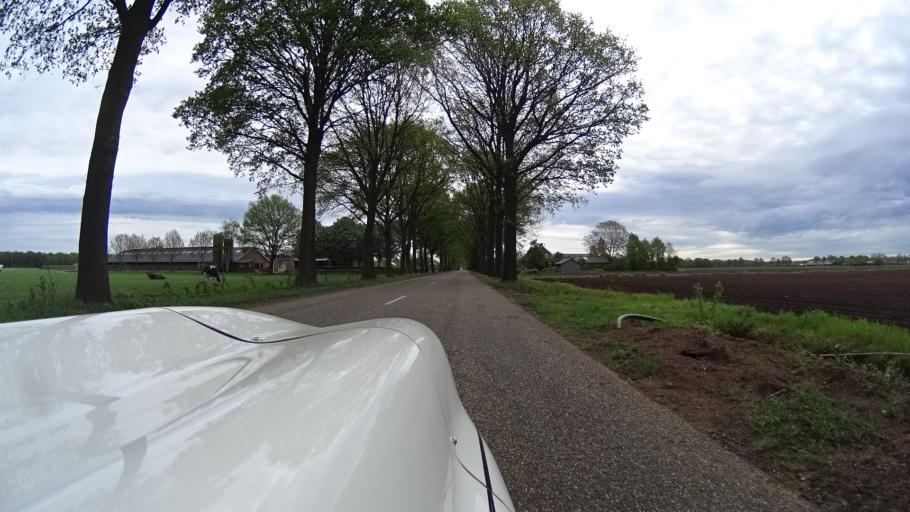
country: NL
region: North Brabant
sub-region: Gemeente Boekel
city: Boekel
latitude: 51.5476
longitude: 5.7340
